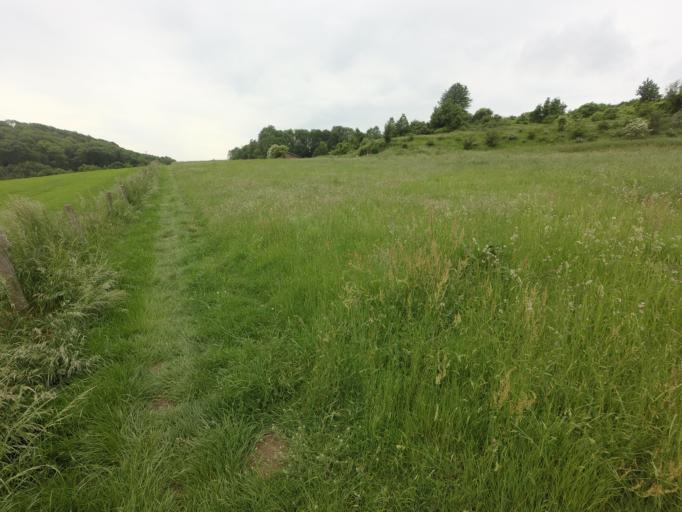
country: NL
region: Limburg
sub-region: Gemeente Voerendaal
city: Ubachsberg
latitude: 50.8605
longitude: 5.9652
